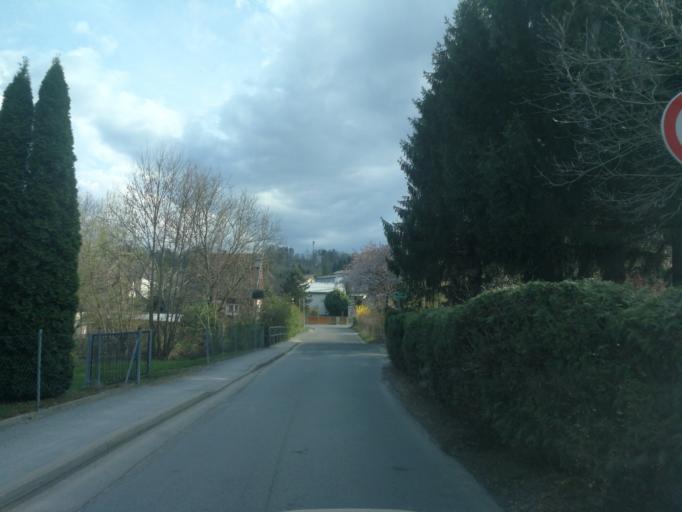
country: AT
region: Styria
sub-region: Graz Stadt
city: Mariatrost
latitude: 47.0742
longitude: 15.5076
